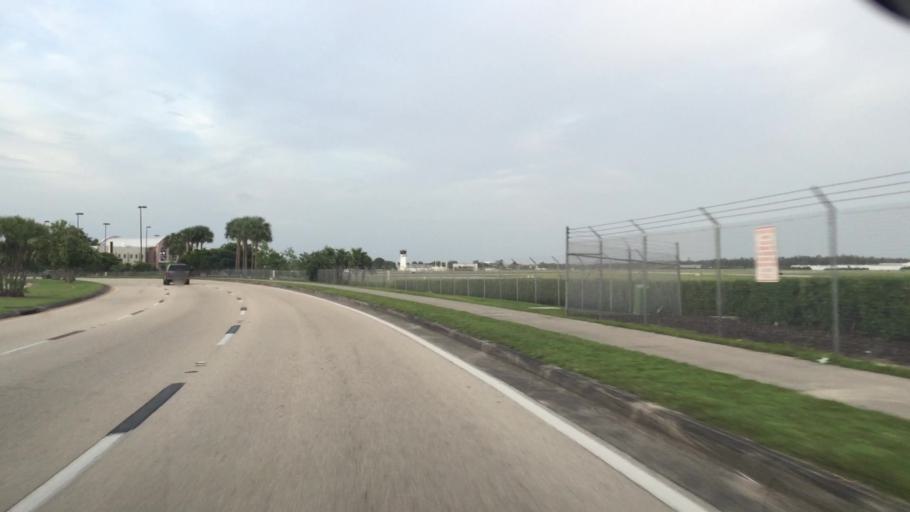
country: US
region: Florida
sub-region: Lee County
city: Pine Manor
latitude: 26.5841
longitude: -81.8691
